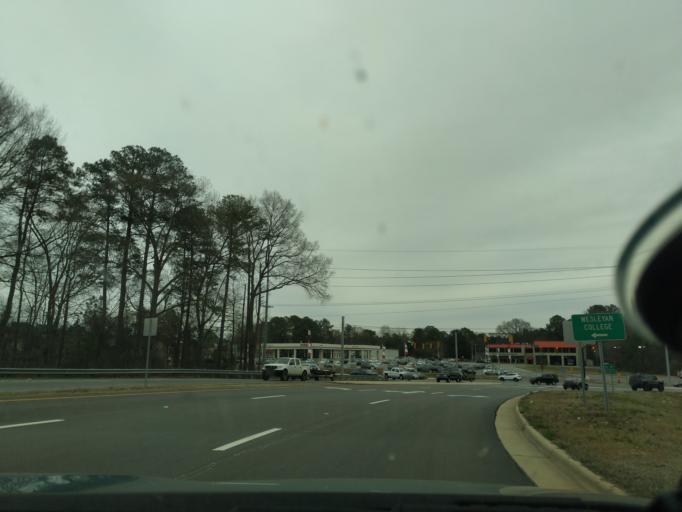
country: US
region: North Carolina
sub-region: Nash County
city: Rocky Mount
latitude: 35.9672
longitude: -77.8178
